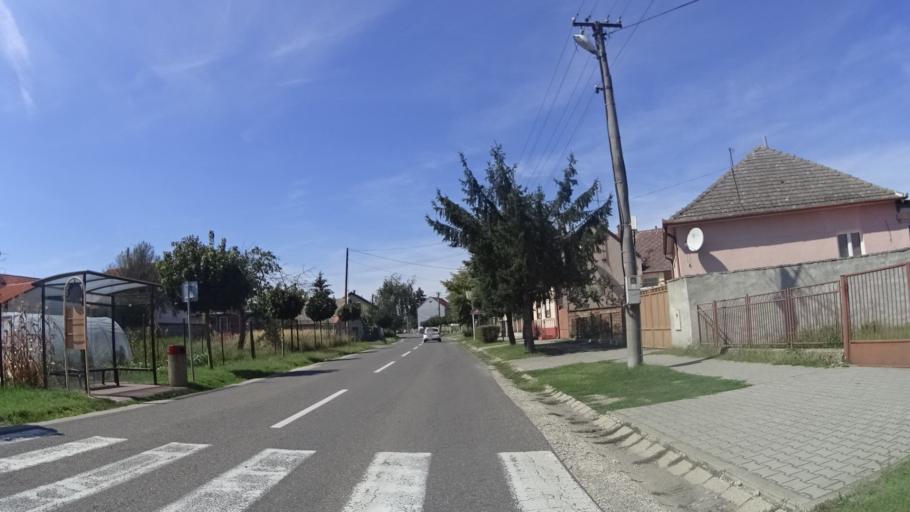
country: AT
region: Lower Austria
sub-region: Politischer Bezirk Ganserndorf
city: Marchegg
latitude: 48.3240
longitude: 16.9120
